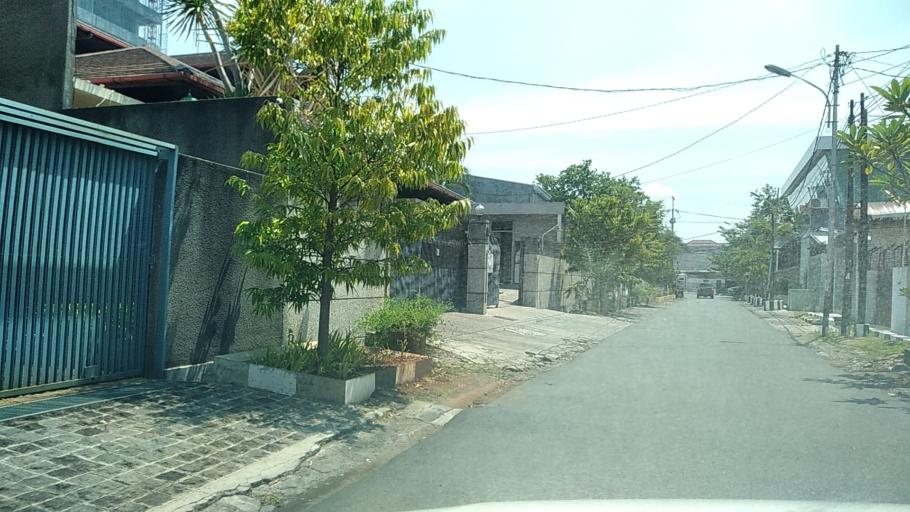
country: ID
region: Central Java
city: Semarang
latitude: -6.9846
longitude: 110.4212
